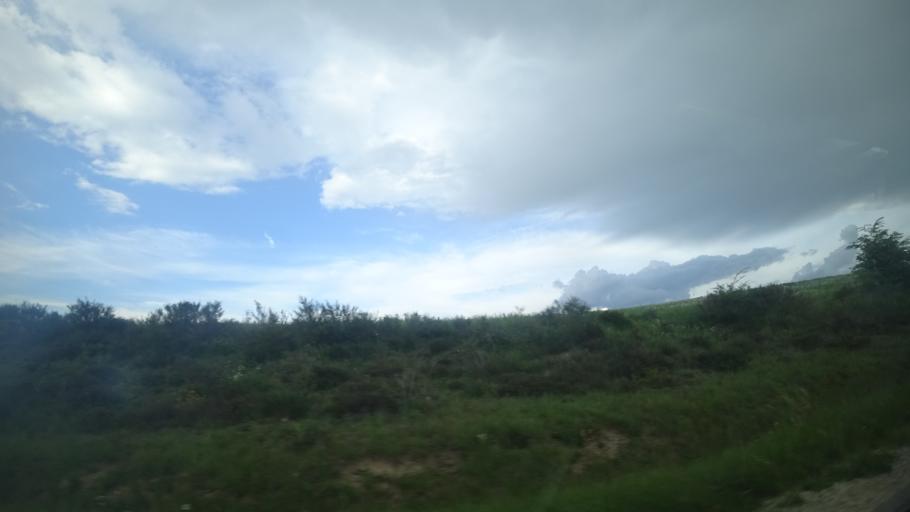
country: FR
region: Midi-Pyrenees
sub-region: Departement de l'Aveyron
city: Severac-le-Chateau
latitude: 44.2463
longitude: 2.9351
